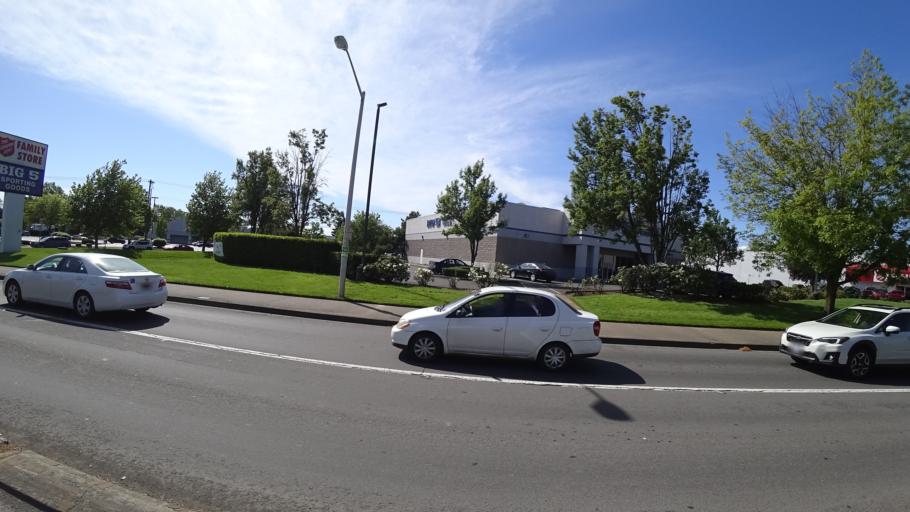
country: US
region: Oregon
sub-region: Washington County
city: Hillsboro
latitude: 45.5081
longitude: -122.9602
